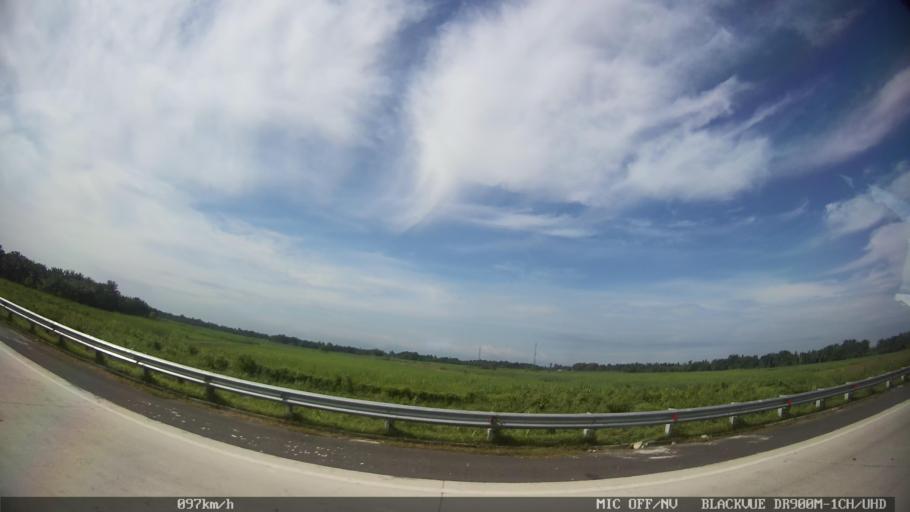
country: ID
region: North Sumatra
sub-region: Kabupaten Langkat
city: Stabat
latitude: 3.7120
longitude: 98.5290
